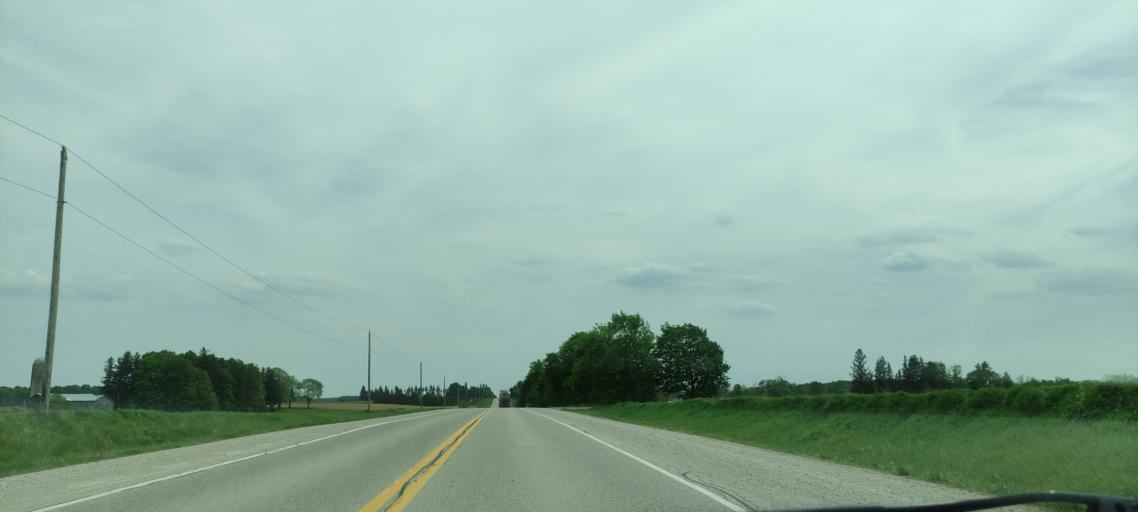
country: CA
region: Ontario
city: Stratford
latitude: 43.2705
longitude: -80.9579
